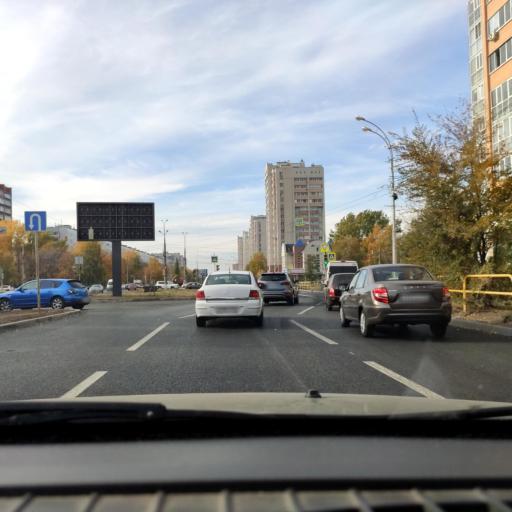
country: RU
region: Samara
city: Tol'yatti
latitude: 53.5135
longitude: 49.2954
